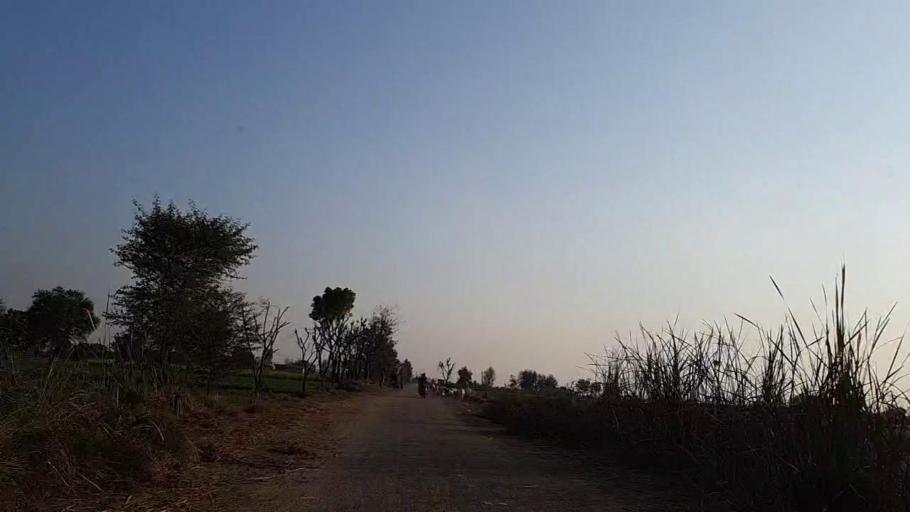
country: PK
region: Sindh
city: Sakrand
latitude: 26.0388
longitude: 68.4378
